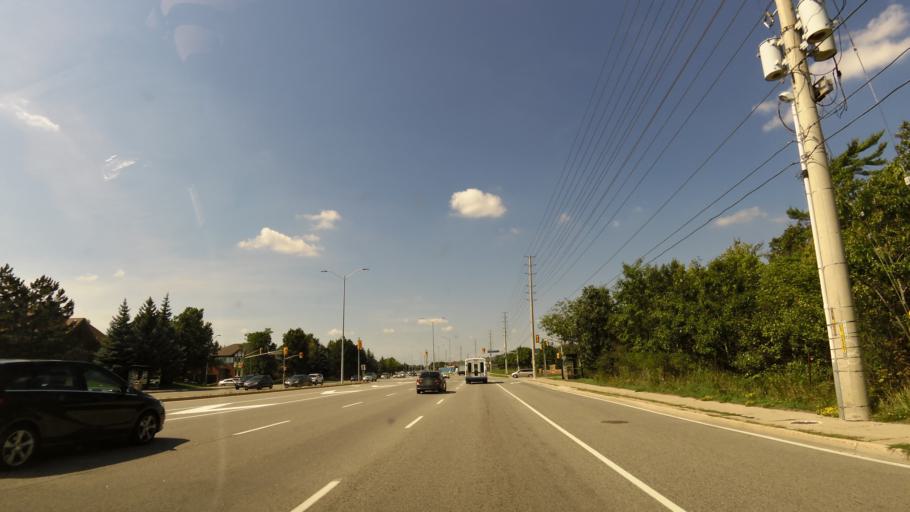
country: CA
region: Ontario
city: Mississauga
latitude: 43.5672
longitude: -79.7179
